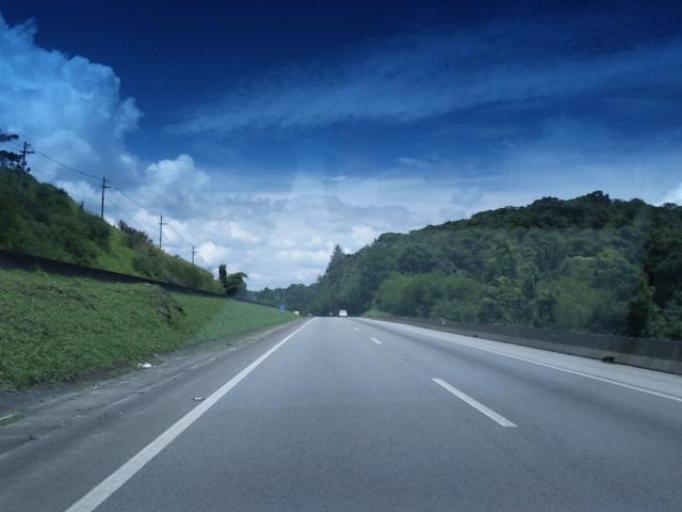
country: BR
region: Sao Paulo
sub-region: Juquitiba
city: Juquitiba
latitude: -23.9401
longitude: -47.0440
